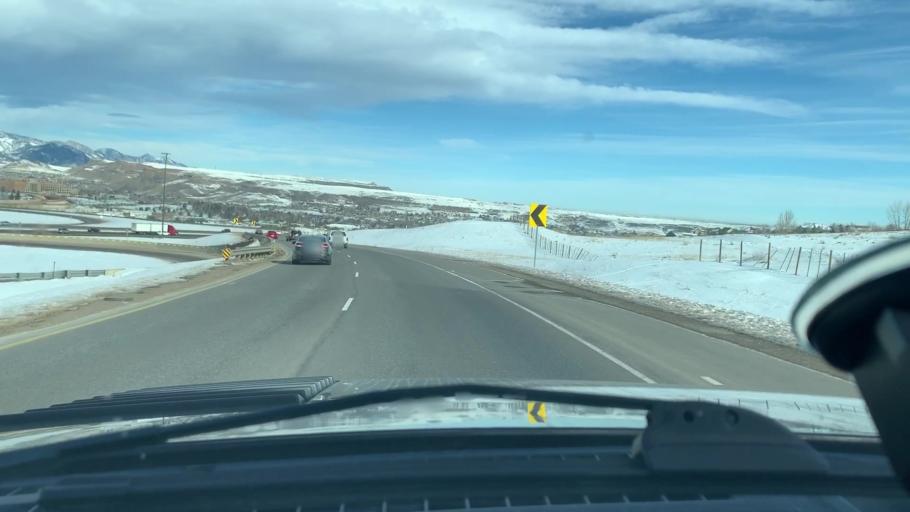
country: US
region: Colorado
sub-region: Jefferson County
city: West Pleasant View
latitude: 39.7117
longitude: -105.1912
